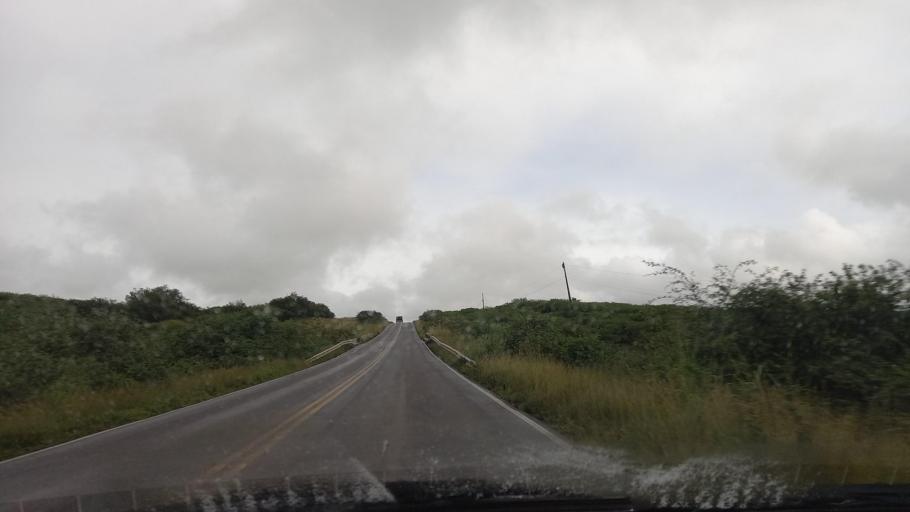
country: BR
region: Pernambuco
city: Garanhuns
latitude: -8.8460
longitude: -36.5244
